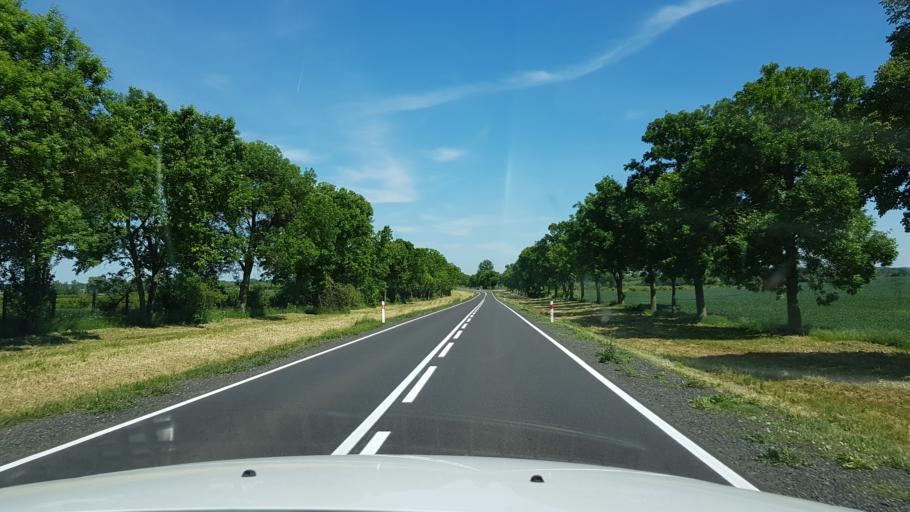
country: PL
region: West Pomeranian Voivodeship
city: Trzcinsko Zdroj
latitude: 52.9611
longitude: 14.5682
